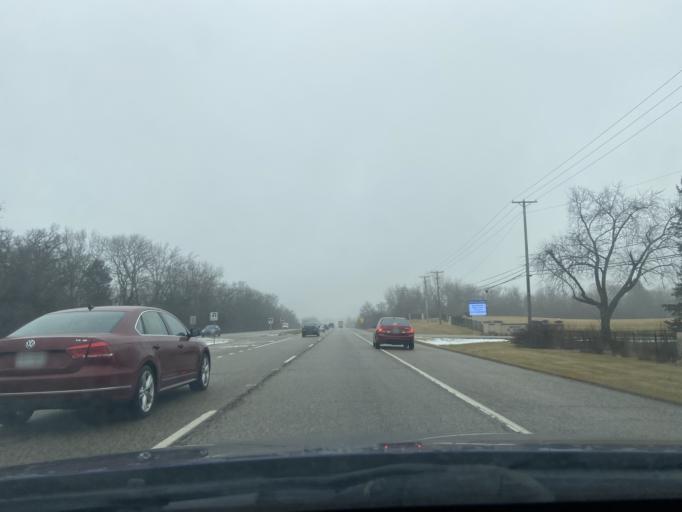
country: US
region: Illinois
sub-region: Lake County
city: Knollwood
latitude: 42.2249
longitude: -88.1114
